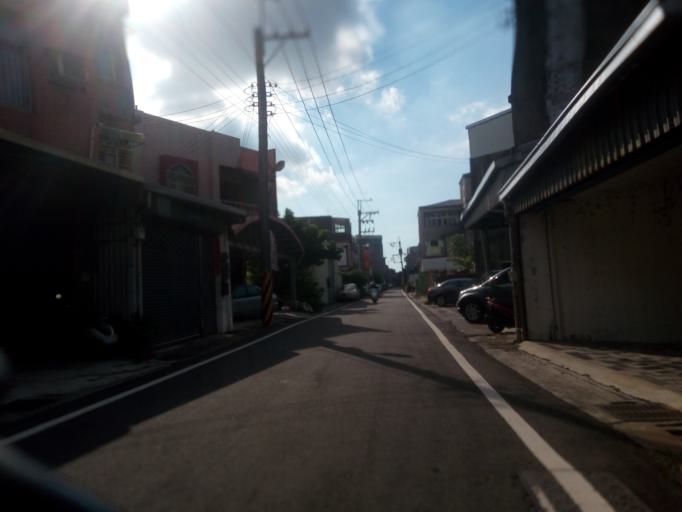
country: TW
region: Taiwan
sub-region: Miaoli
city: Miaoli
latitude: 24.6916
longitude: 120.8755
